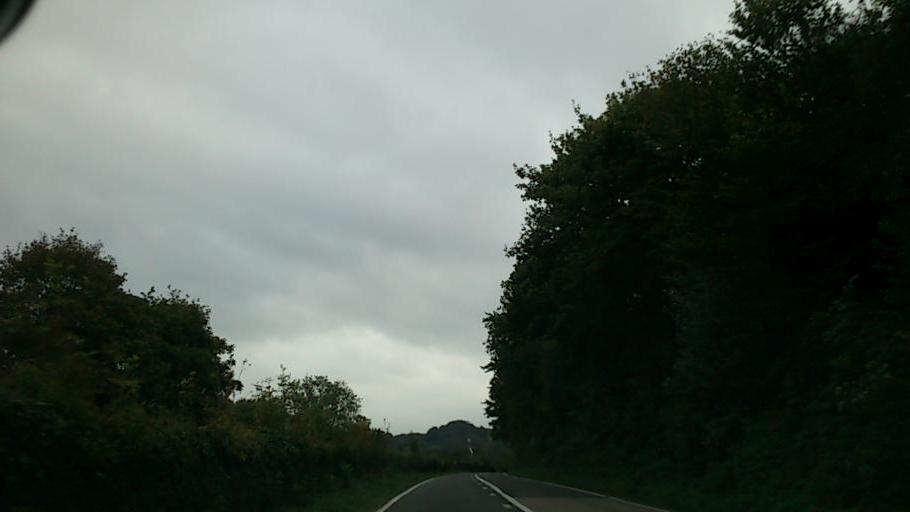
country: GB
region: Wales
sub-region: Sir Powys
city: Machynlleth
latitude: 52.5770
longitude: -3.9061
